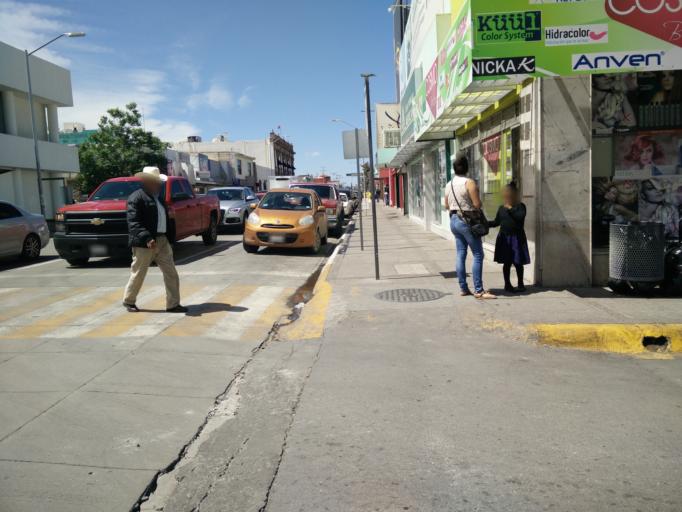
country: MX
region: Chihuahua
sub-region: Chihuahua
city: Chihuahua
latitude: 28.6351
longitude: -106.0767
